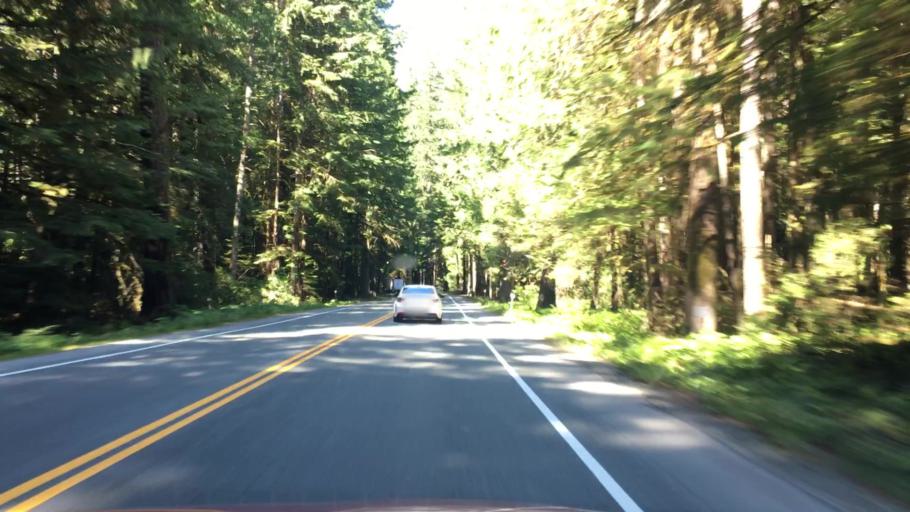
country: CA
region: British Columbia
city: Port Alberni
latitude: 49.2767
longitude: -124.6750
